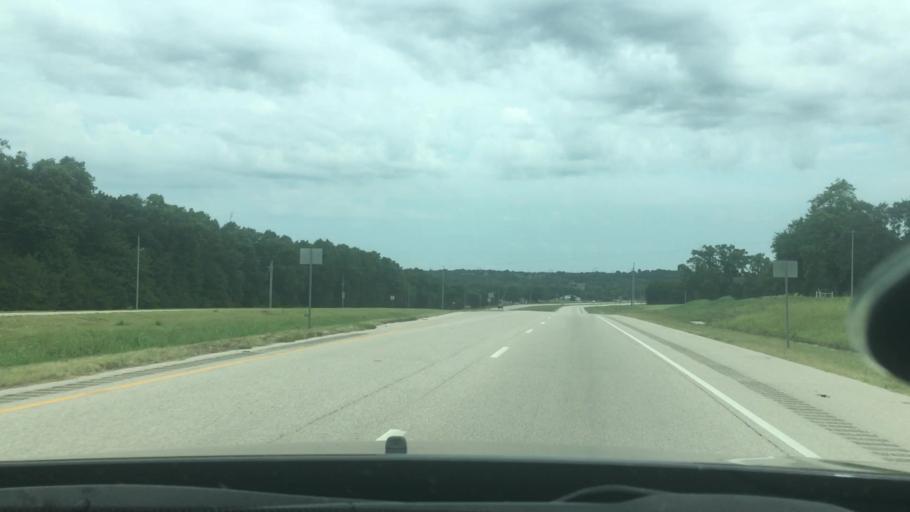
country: US
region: Oklahoma
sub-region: Pontotoc County
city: Byng
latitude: 34.9180
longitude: -96.6816
